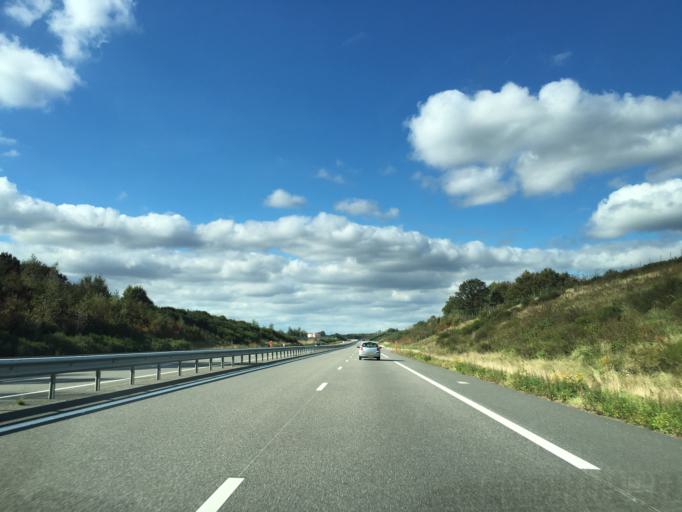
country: FR
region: Lorraine
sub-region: Departement de Meurthe-et-Moselle
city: Baccarat
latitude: 48.5191
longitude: 6.6468
